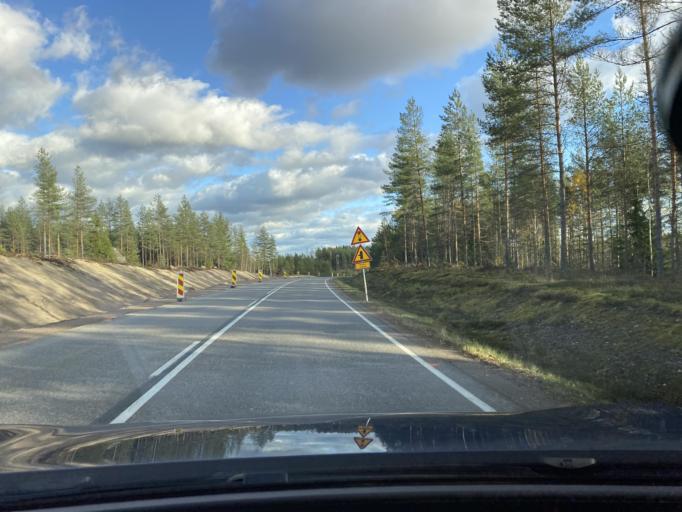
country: FI
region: Paijanne Tavastia
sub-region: Lahti
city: Jaervelae
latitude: 60.8439
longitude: 25.3034
